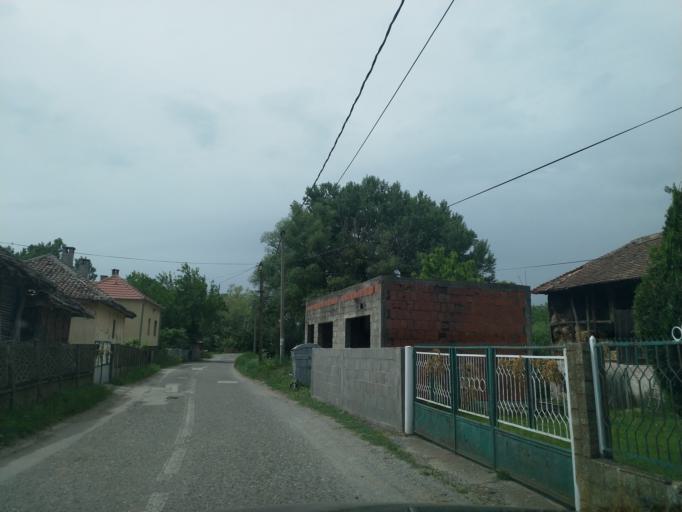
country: RS
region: Central Serbia
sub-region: Pomoravski Okrug
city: Paracin
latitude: 43.8602
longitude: 21.5905
